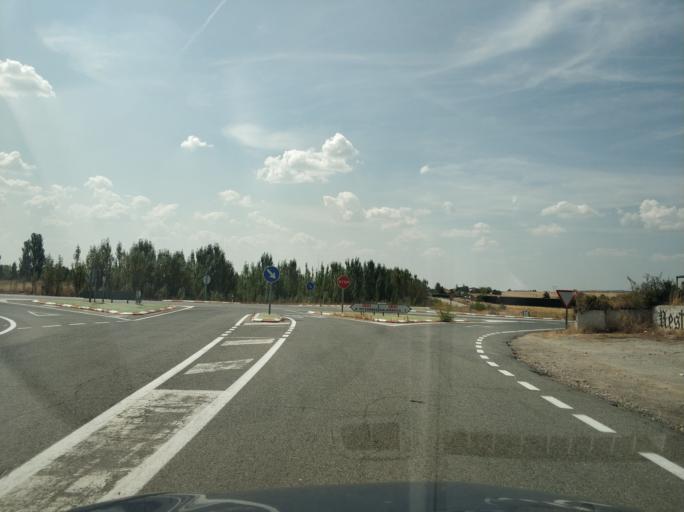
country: ES
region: Castille and Leon
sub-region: Provincia de Salamanca
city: Arapiles
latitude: 40.8956
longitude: -5.6638
